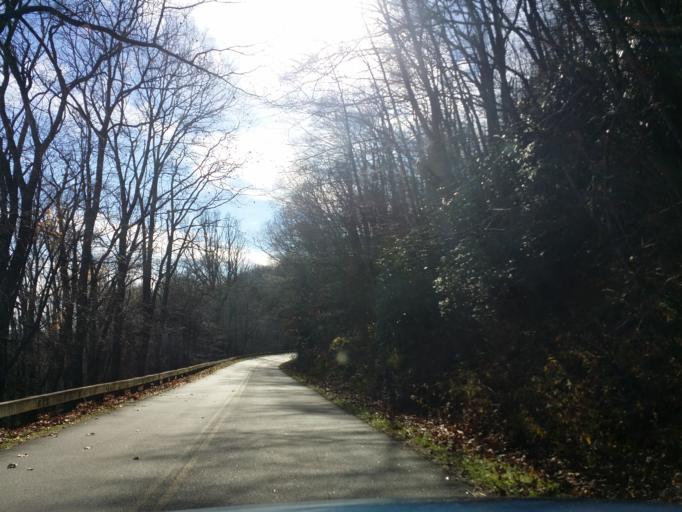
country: US
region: North Carolina
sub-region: Buncombe County
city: Black Mountain
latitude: 35.7115
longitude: -82.2426
